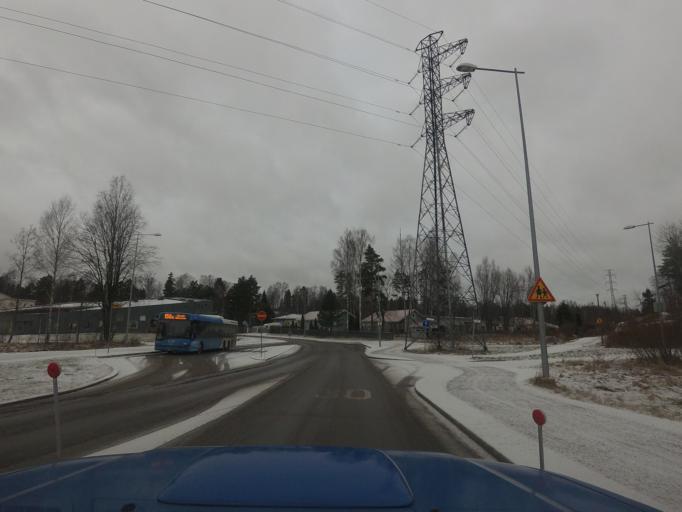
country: FI
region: Uusimaa
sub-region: Helsinki
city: Espoo
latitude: 60.1662
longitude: 24.6330
